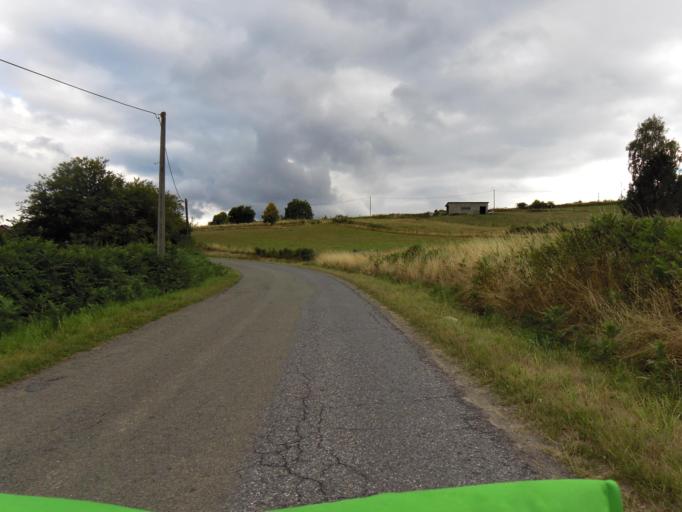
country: BE
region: Wallonia
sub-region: Province de Namur
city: Bievre
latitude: 49.8739
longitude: 4.9810
